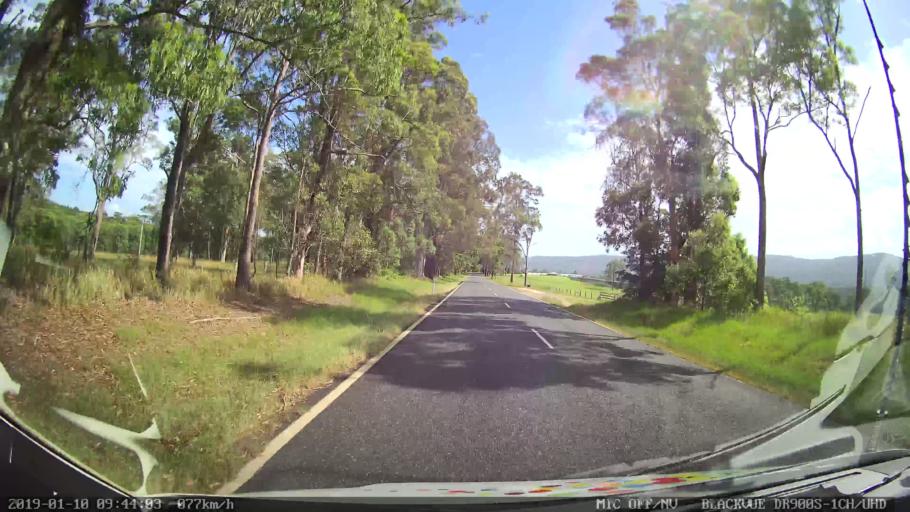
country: AU
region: New South Wales
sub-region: Coffs Harbour
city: Nana Glen
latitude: -30.1213
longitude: 153.0033
